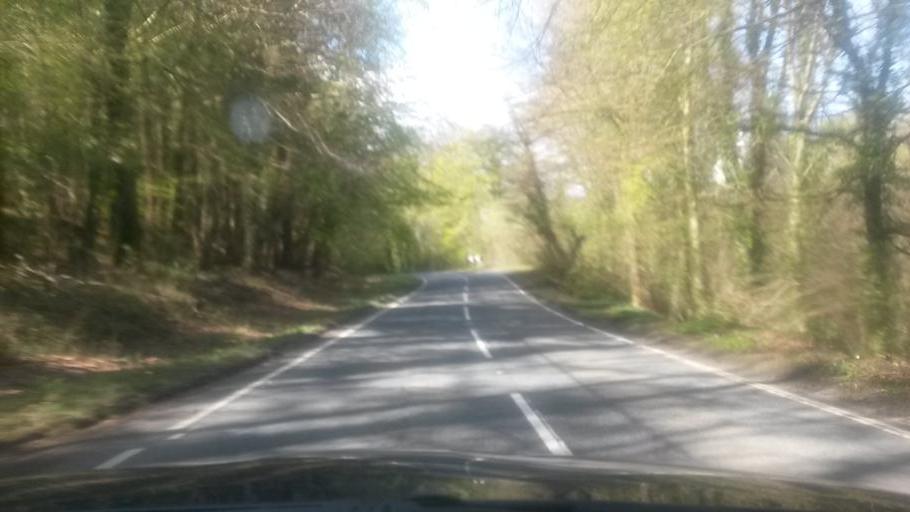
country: GB
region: Northern Ireland
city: Irvinestown
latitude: 54.4148
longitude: -7.7281
